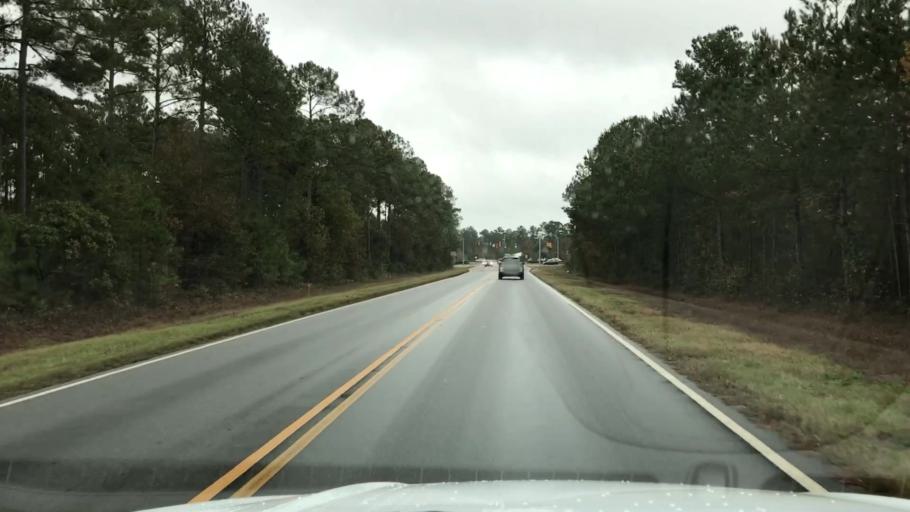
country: US
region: South Carolina
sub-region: Horry County
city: Myrtle Beach
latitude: 33.7542
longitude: -78.8701
